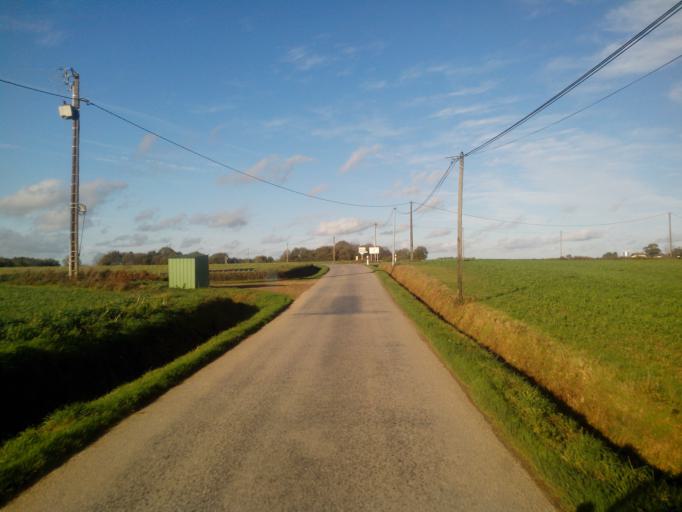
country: FR
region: Brittany
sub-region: Departement du Morbihan
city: Guilliers
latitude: 48.0585
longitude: -2.4002
